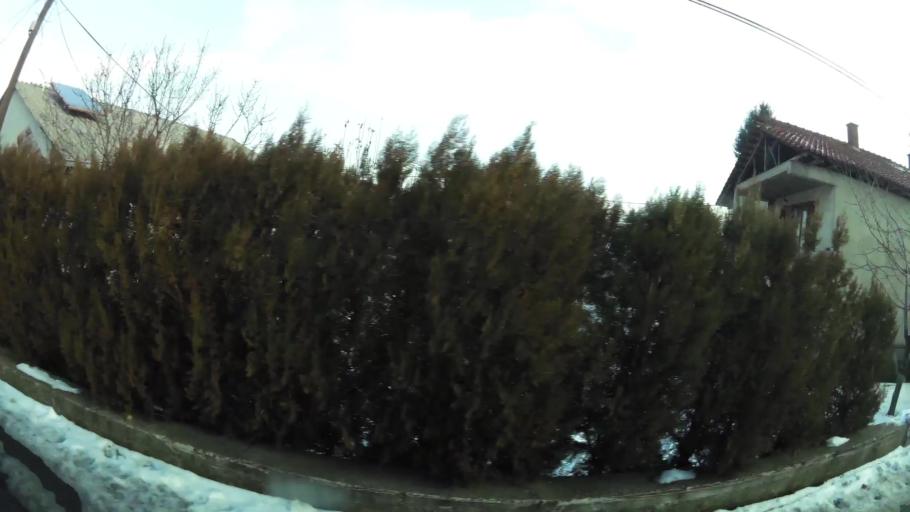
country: MK
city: Creshevo
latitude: 42.0112
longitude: 21.4983
